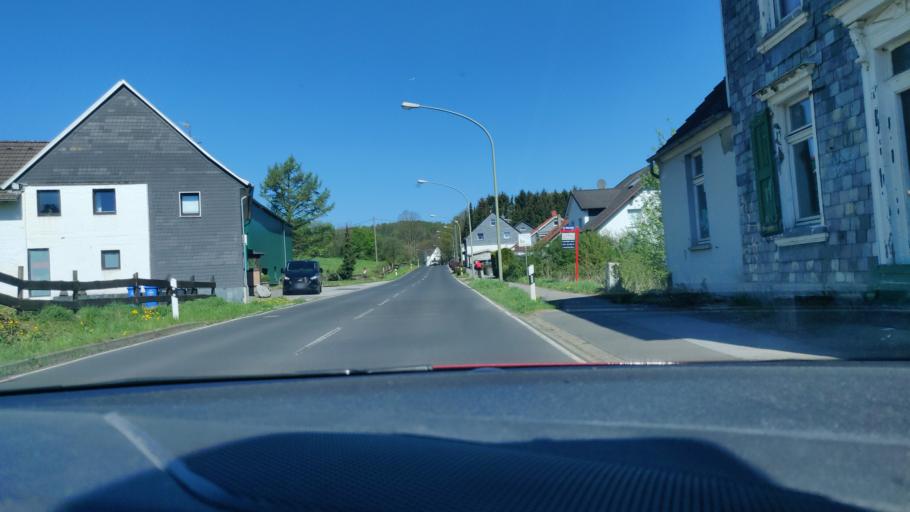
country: DE
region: North Rhine-Westphalia
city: Wulfrath
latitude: 51.2807
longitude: 7.0728
